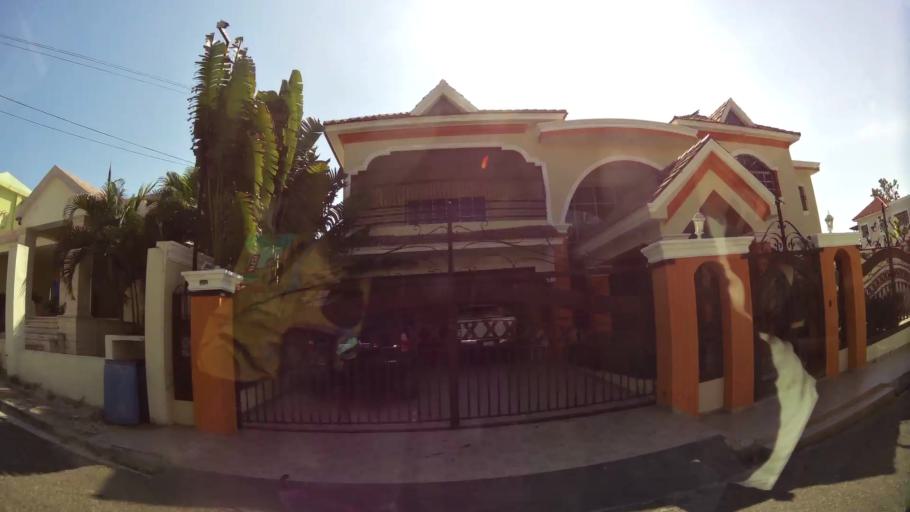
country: DO
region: Nacional
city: Bella Vista
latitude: 18.4608
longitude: -69.9825
